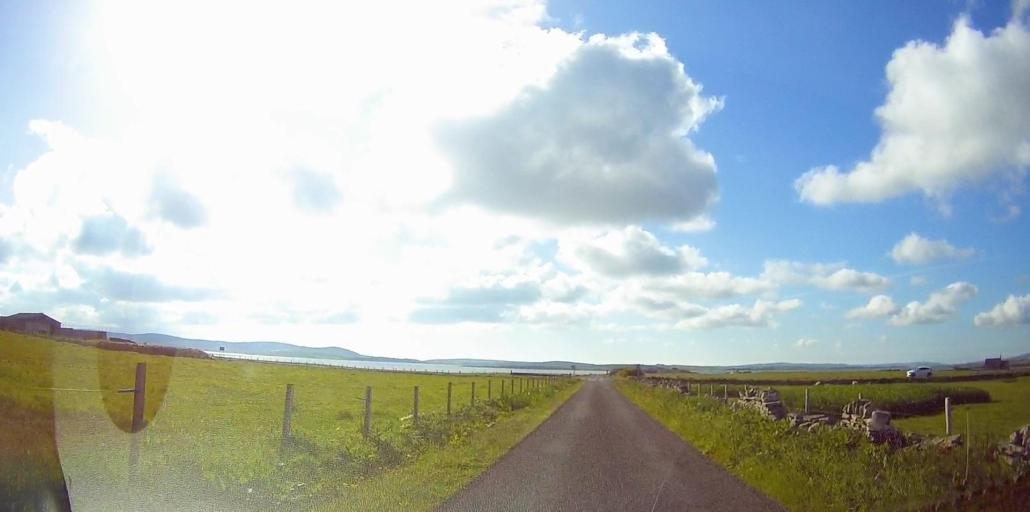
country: GB
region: Scotland
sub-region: Orkney Islands
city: Stromness
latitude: 58.9891
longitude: -3.1982
